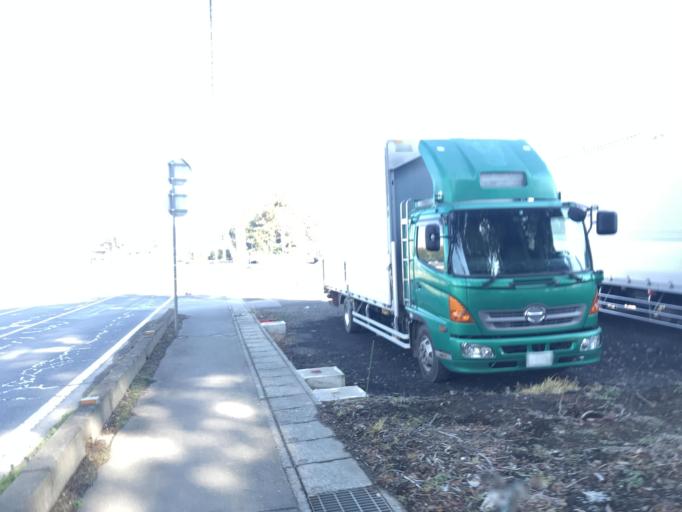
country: JP
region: Tochigi
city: Oyama
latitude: 36.2349
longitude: 139.8254
